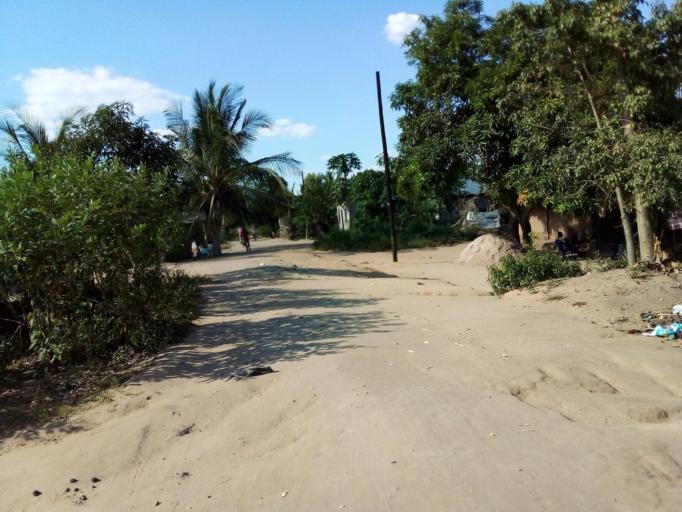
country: MZ
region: Zambezia
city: Quelimane
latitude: -17.6013
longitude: 36.8239
